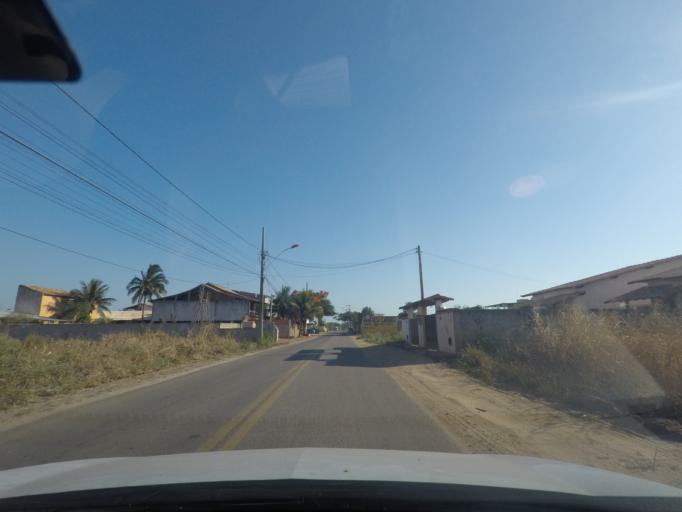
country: BR
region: Rio de Janeiro
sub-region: Marica
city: Marica
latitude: -22.9578
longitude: -42.9425
